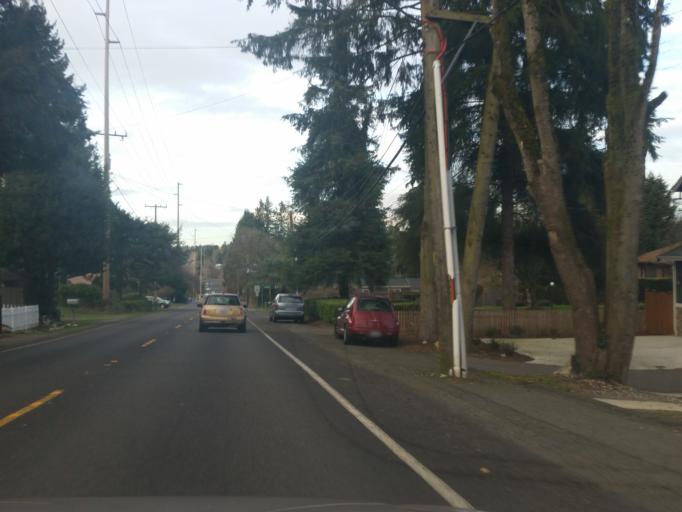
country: US
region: Washington
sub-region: King County
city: Shoreline
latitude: 47.7345
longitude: -122.3289
